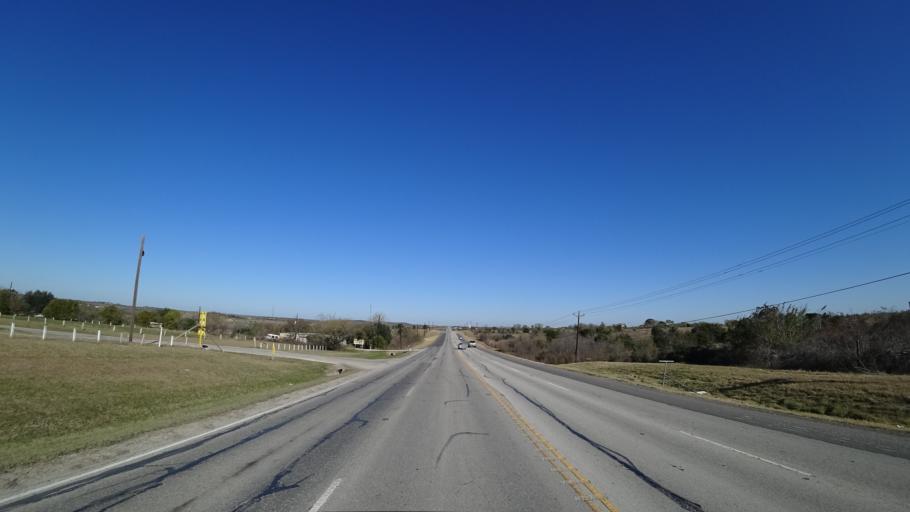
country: US
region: Texas
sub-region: Travis County
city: Onion Creek
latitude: 30.1214
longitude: -97.6954
